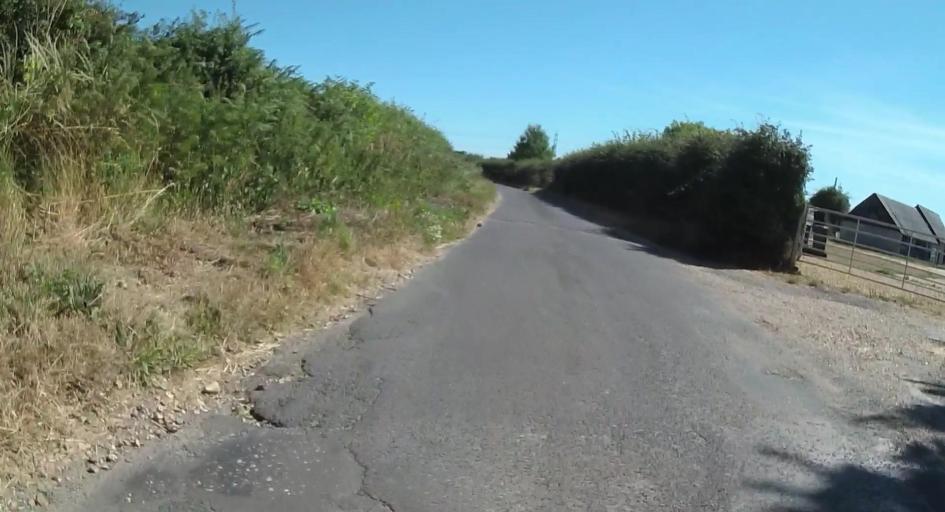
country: GB
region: England
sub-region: Dorset
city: Bovington Camp
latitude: 50.7313
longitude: -2.2041
